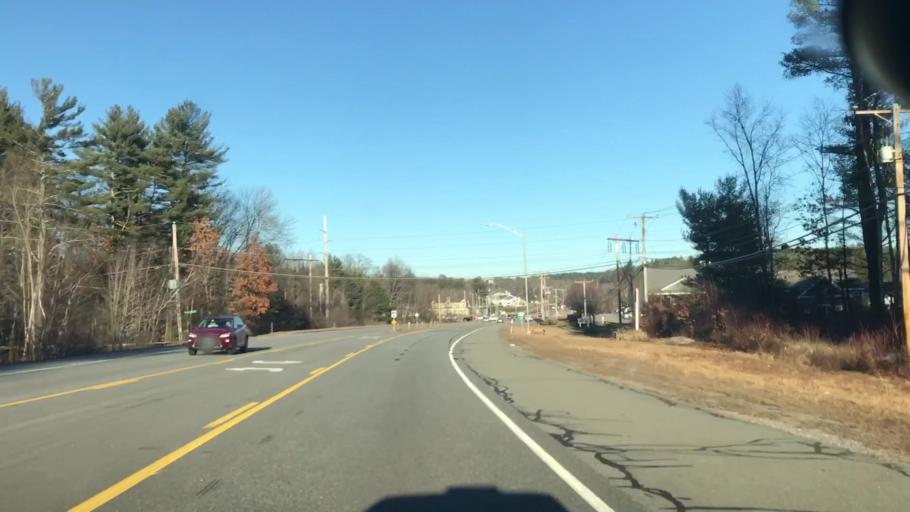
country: US
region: New Hampshire
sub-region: Hillsborough County
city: Bedford
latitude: 42.9353
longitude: -71.5292
